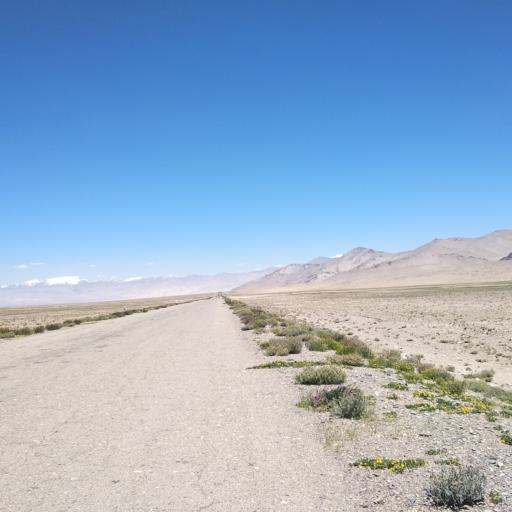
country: TJ
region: Gorno-Badakhshan
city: Murghob
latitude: 38.8990
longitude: 73.4968
